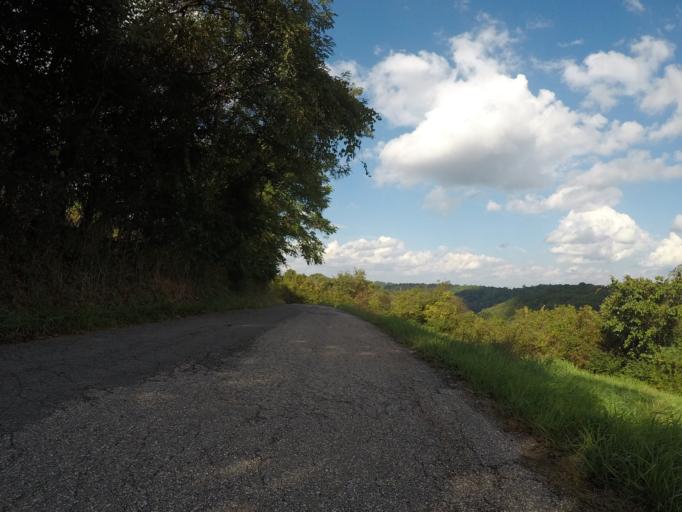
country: US
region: West Virginia
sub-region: Wayne County
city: Lavalette
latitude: 38.3661
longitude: -82.4734
